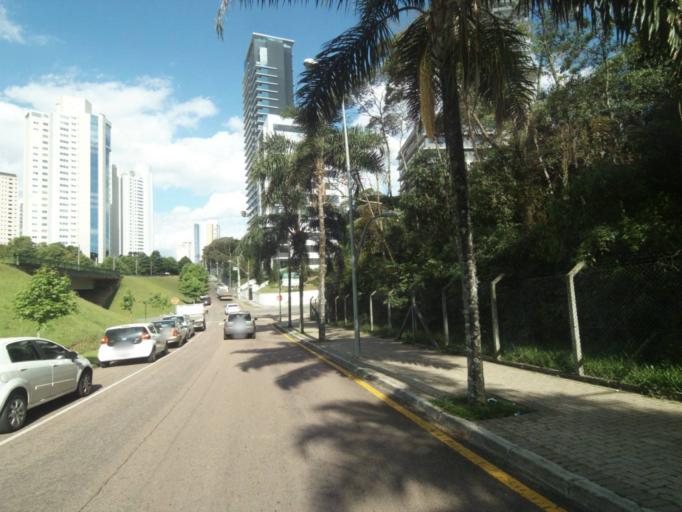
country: BR
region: Parana
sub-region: Curitiba
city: Curitiba
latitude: -25.4409
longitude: -49.3406
